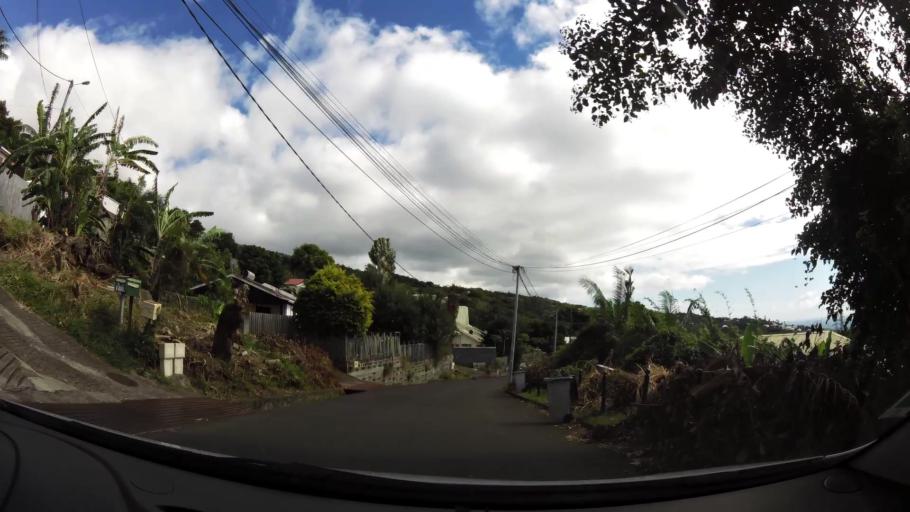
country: RE
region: Reunion
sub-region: Reunion
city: Saint-Denis
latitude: -20.9278
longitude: 55.4877
